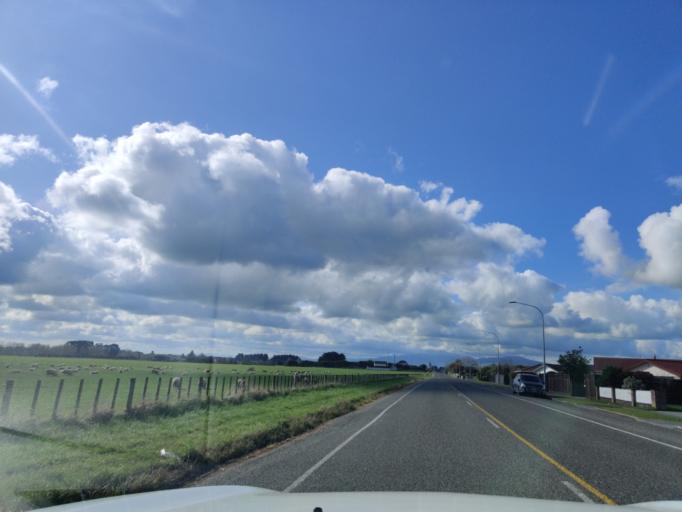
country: NZ
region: Manawatu-Wanganui
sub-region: Palmerston North City
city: Palmerston North
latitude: -40.3227
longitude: 175.6475
